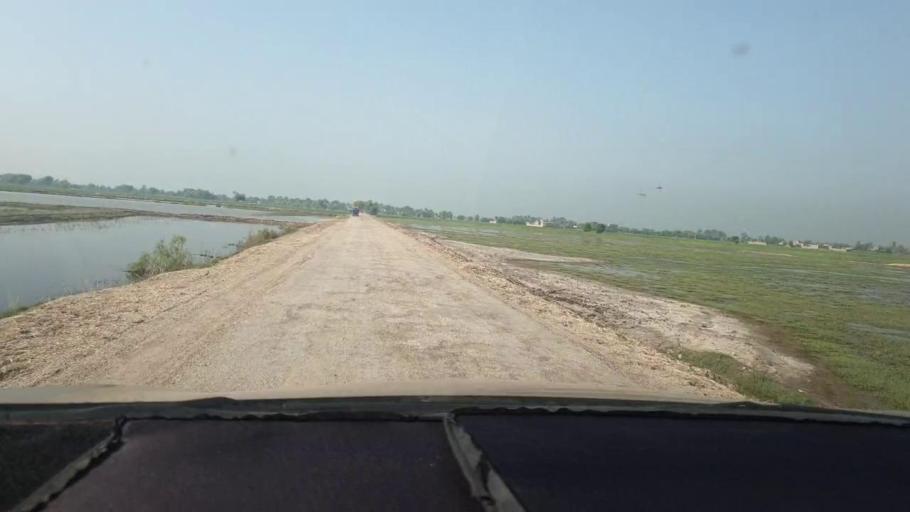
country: PK
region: Sindh
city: Kambar
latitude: 27.5771
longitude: 68.0890
